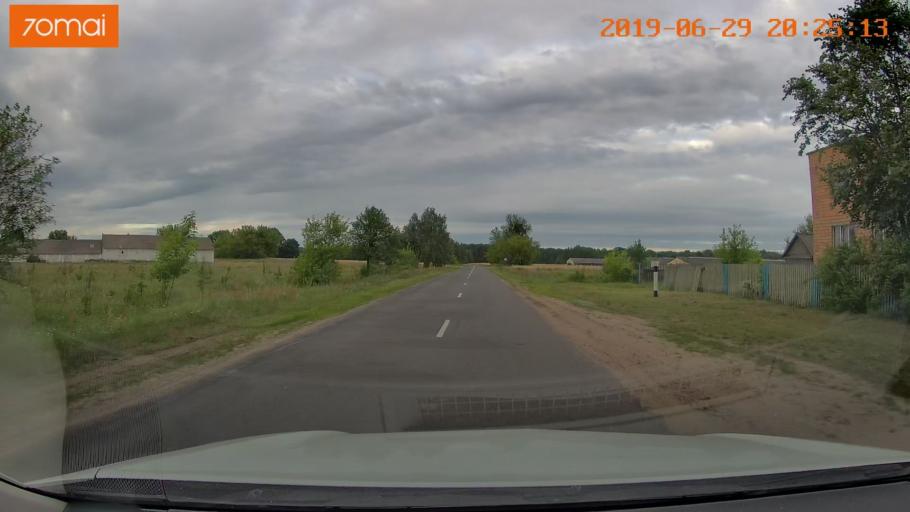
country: BY
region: Brest
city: Asnyezhytsy
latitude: 52.4563
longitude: 26.2770
